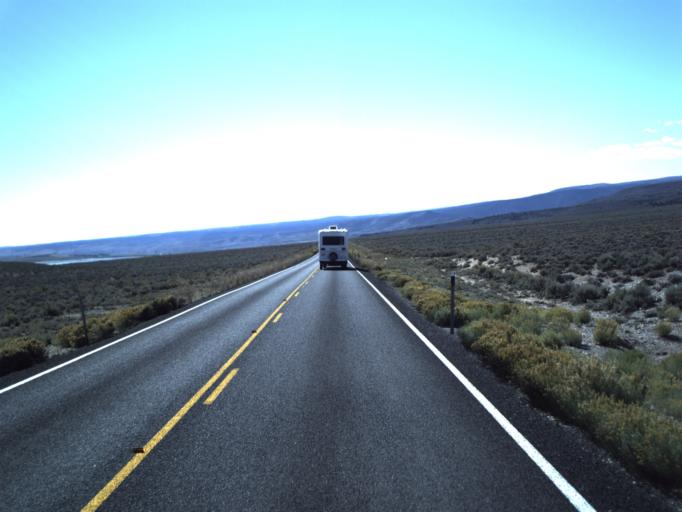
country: US
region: Utah
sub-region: Piute County
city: Junction
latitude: 38.2175
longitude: -112.0010
